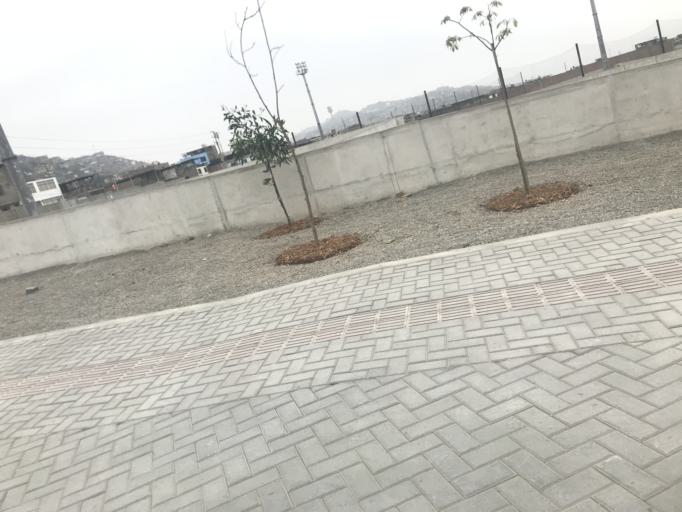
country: PE
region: Lima
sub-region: Lima
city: Surco
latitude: -12.1481
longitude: -76.9506
